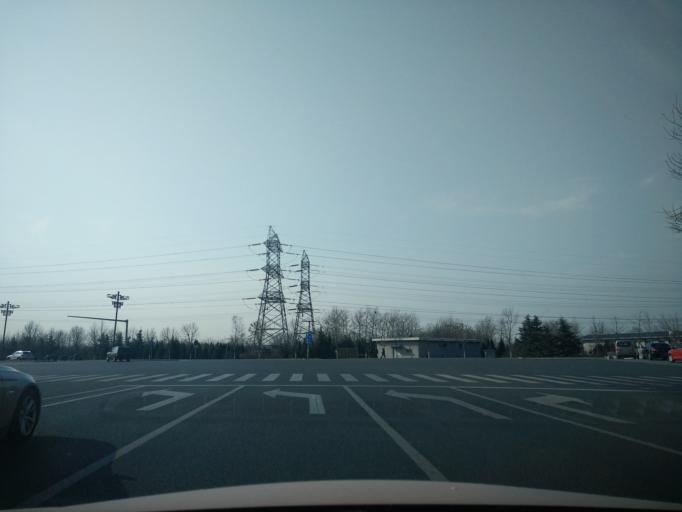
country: CN
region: Beijing
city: Jiugong
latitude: 39.7777
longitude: 116.4749
